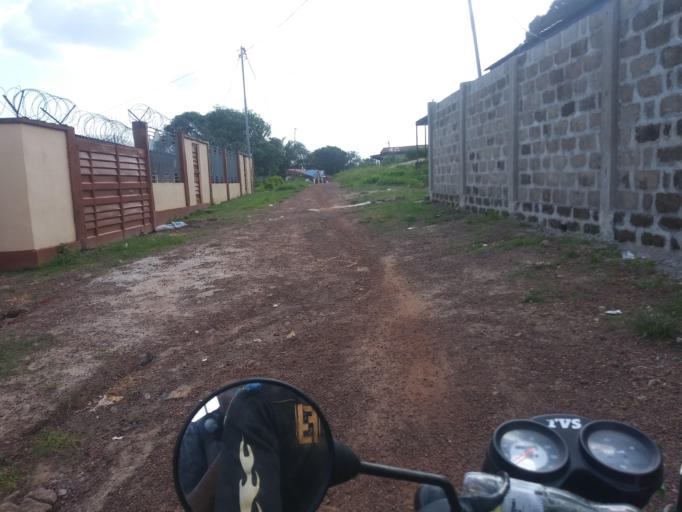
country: SL
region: Northern Province
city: Makeni
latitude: 8.8907
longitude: -12.0344
